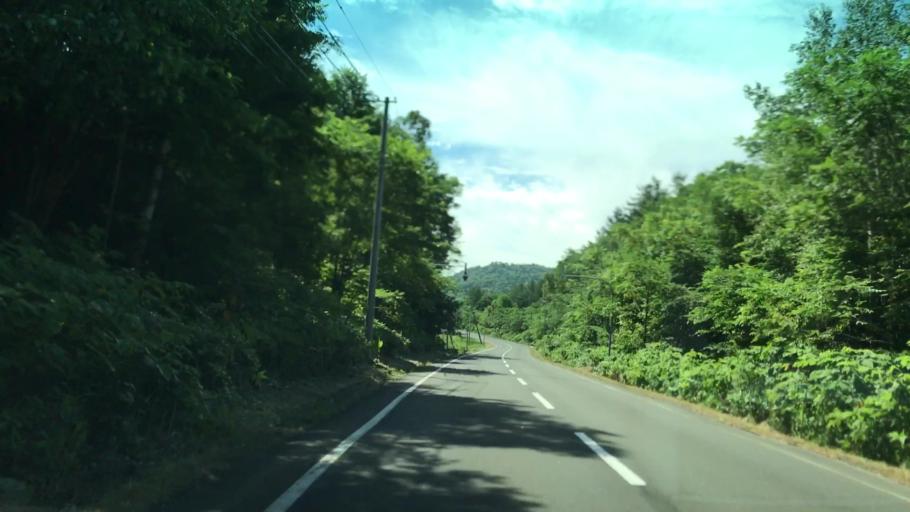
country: JP
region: Hokkaido
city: Shimo-furano
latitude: 42.9611
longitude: 142.4284
